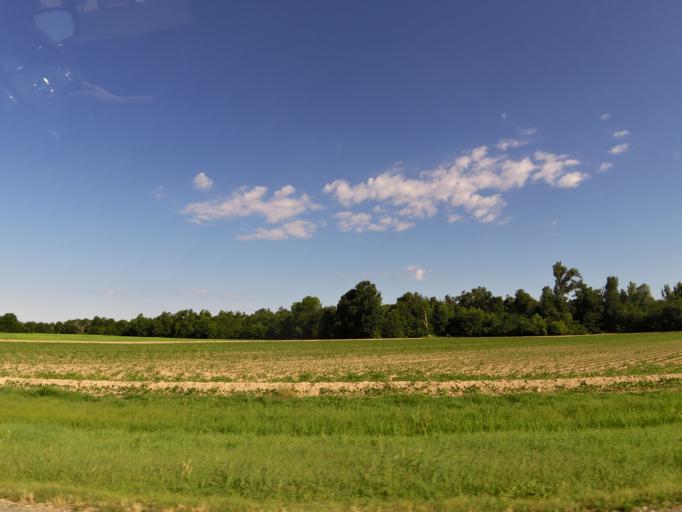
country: US
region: Arkansas
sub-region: Clay County
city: Corning
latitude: 36.4728
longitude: -90.5609
